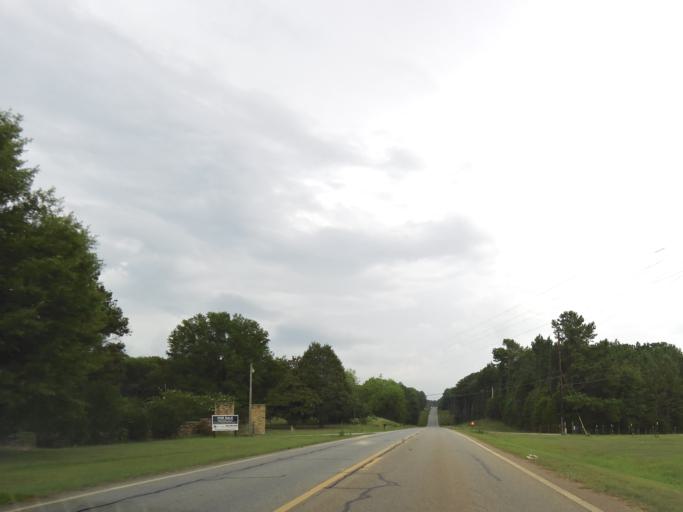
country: US
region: Georgia
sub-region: Bibb County
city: West Point
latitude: 32.8607
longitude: -83.8024
